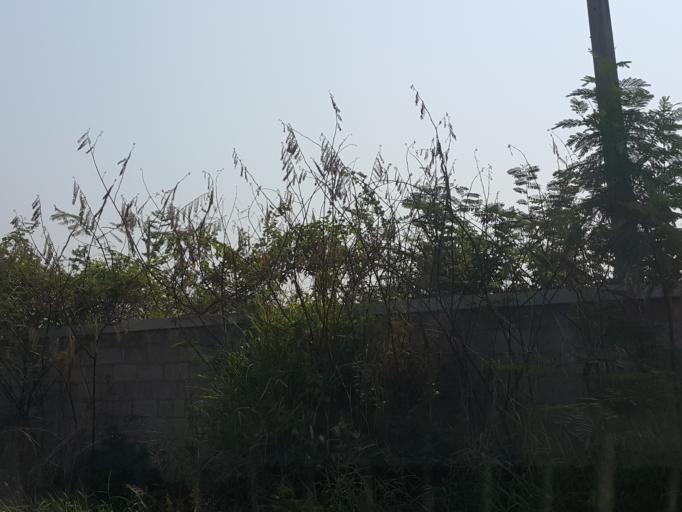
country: TH
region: Chiang Mai
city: Hang Dong
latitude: 18.7132
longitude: 98.9645
